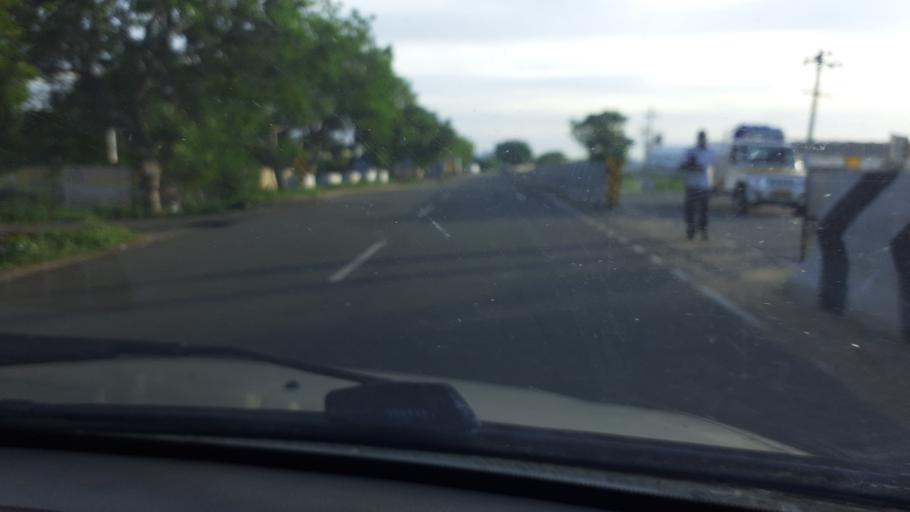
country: IN
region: Tamil Nadu
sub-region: Tirunelveli Kattabo
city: Tirunelveli
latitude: 8.6711
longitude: 77.7187
